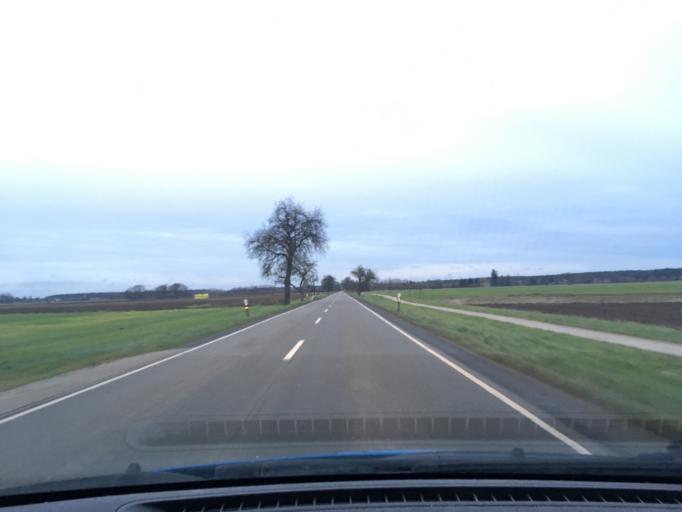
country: DE
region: Lower Saxony
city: Neu Darchau
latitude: 53.2671
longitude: 10.9223
